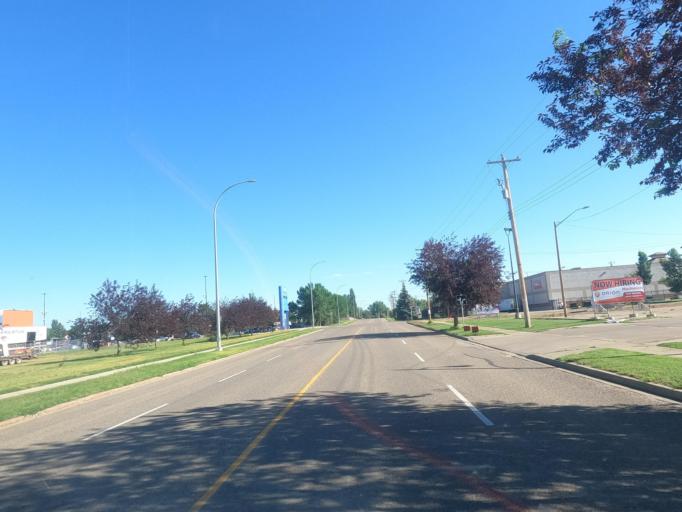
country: CA
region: Alberta
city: Brooks
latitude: 50.5772
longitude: -111.9001
